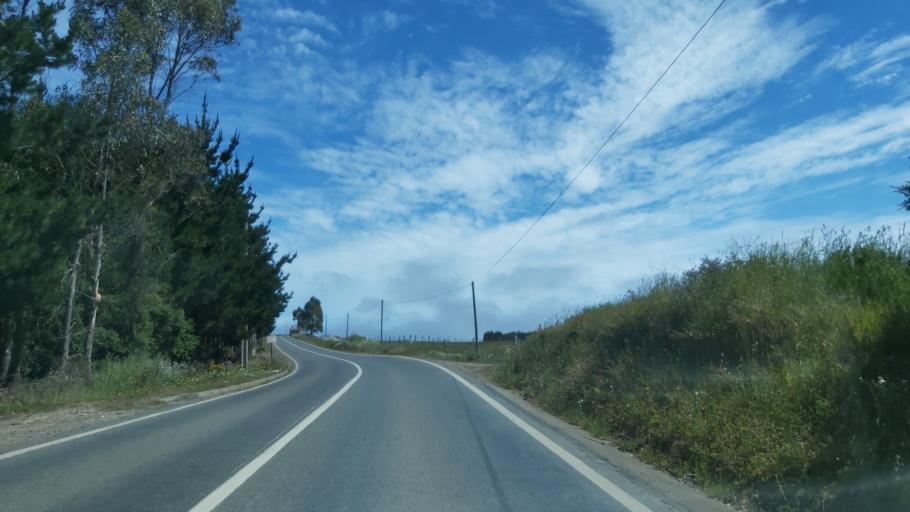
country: CL
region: Maule
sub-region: Provincia de Talca
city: Constitucion
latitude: -35.5728
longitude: -72.6026
